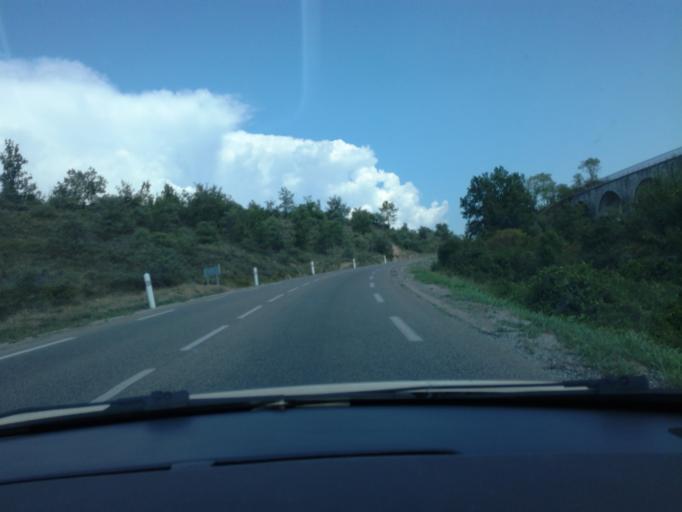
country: FR
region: Rhone-Alpes
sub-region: Departement de l'Ardeche
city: Ruoms
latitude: 44.4935
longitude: 4.3808
